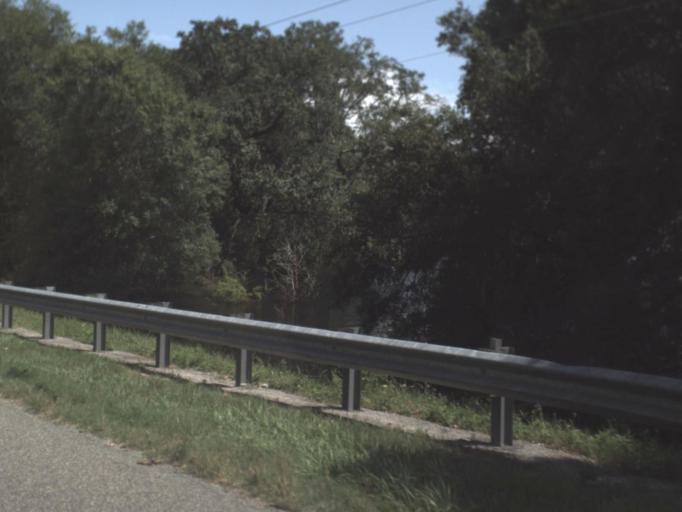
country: US
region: Florida
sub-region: Lafayette County
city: Mayo
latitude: 30.0152
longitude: -83.0397
